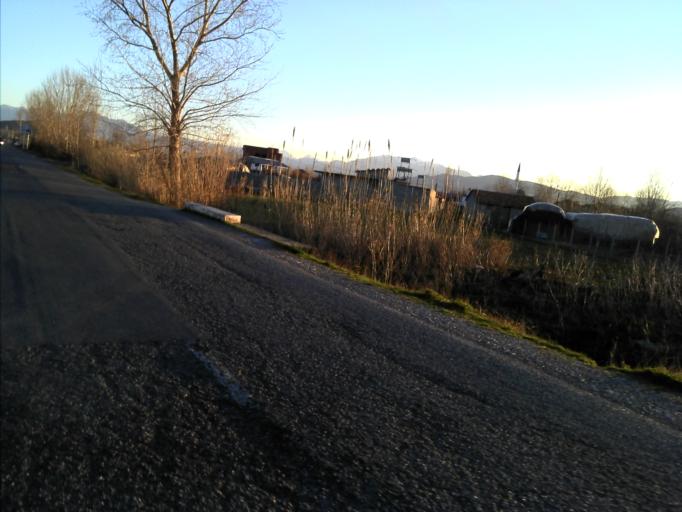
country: AL
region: Shkoder
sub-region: Rrethi i Shkodres
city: Berdica e Madhe
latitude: 41.9777
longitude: 19.4786
